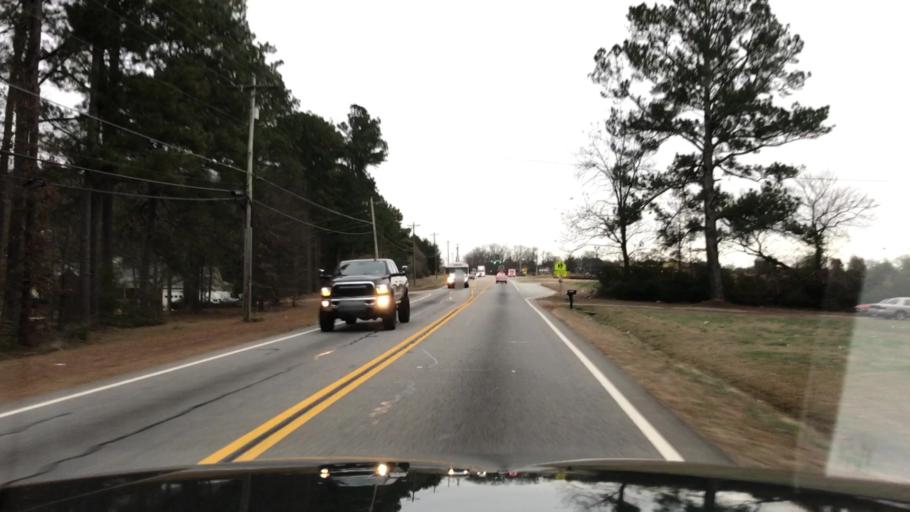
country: US
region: Georgia
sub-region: Walton County
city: Monroe
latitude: 33.8197
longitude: -83.7316
